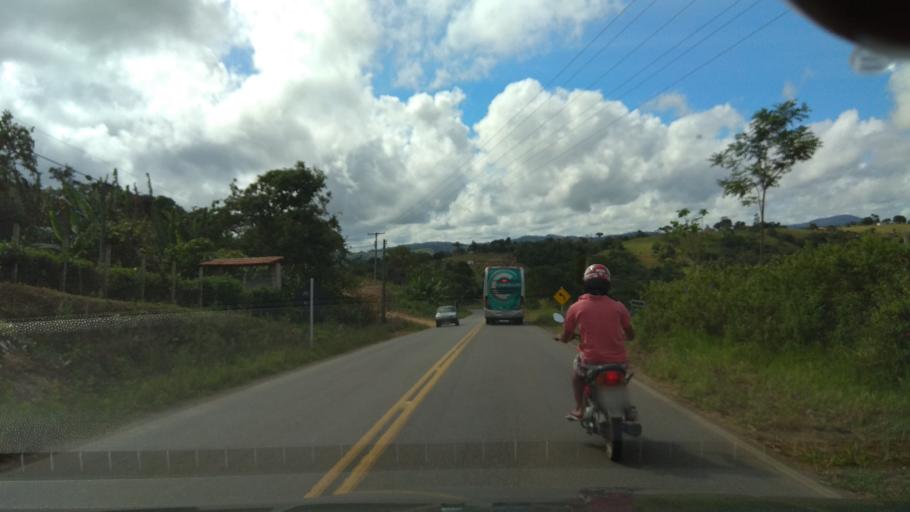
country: BR
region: Bahia
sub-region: Mutuipe
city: Mutuipe
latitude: -13.2127
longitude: -39.4787
